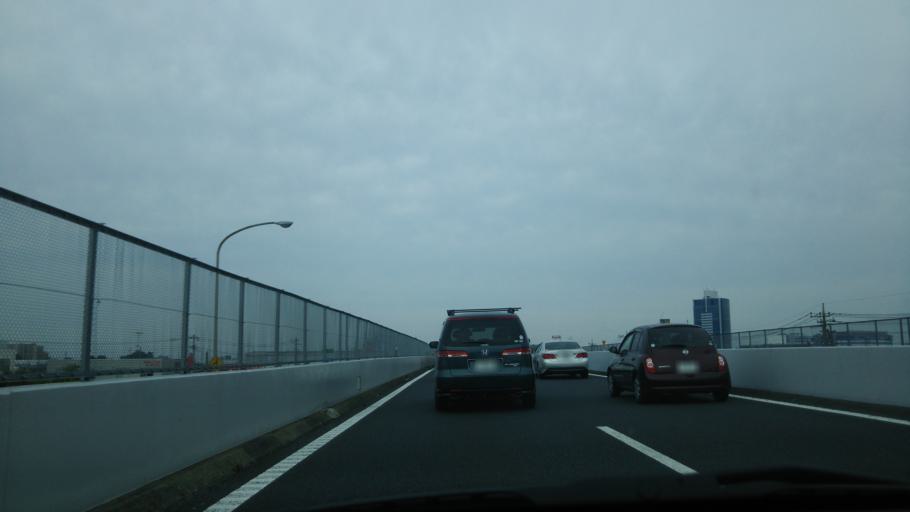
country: JP
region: Kanagawa
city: Atsugi
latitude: 35.4158
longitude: 139.3499
